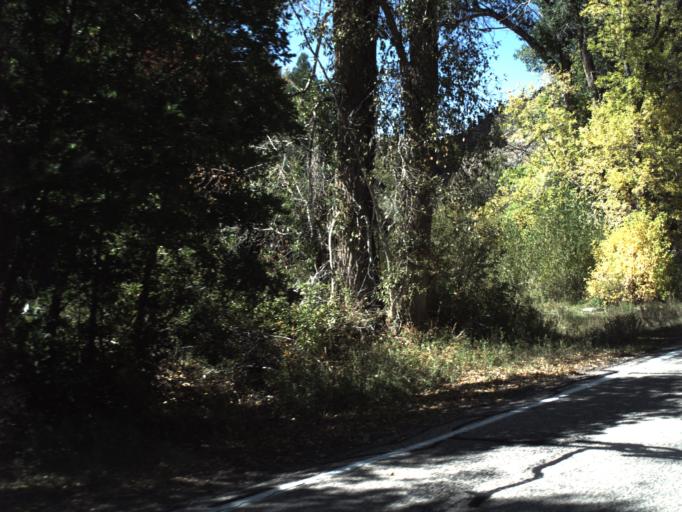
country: US
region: Utah
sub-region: Beaver County
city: Beaver
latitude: 38.2723
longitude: -112.5511
